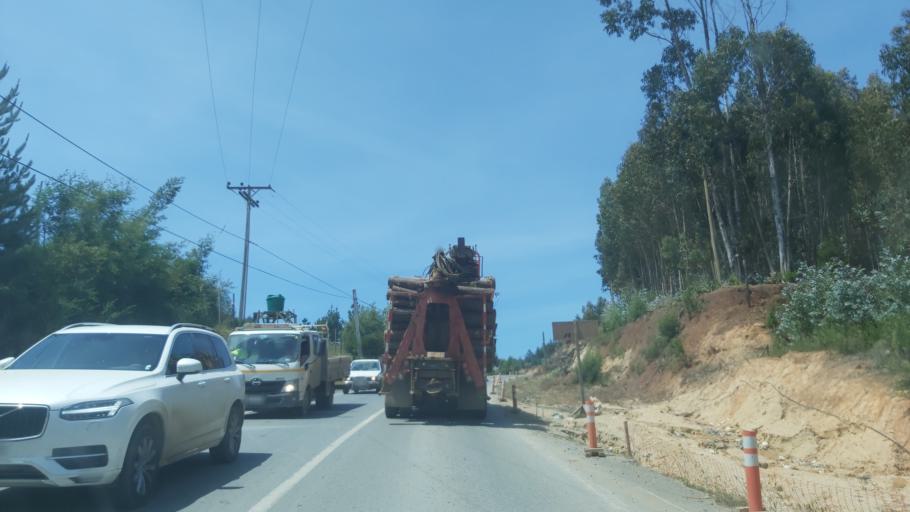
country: CL
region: Maule
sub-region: Provincia de Talca
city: Constitucion
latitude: -35.4436
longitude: -72.4631
